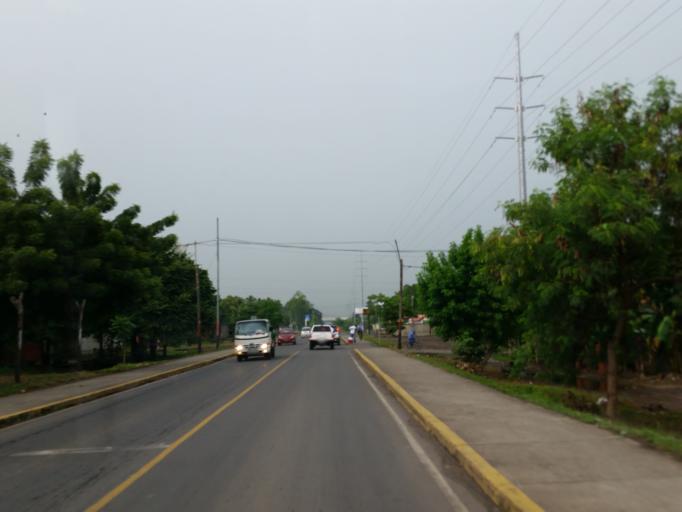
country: NI
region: Chinandega
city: Chinandega
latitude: 12.6493
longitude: -87.1258
